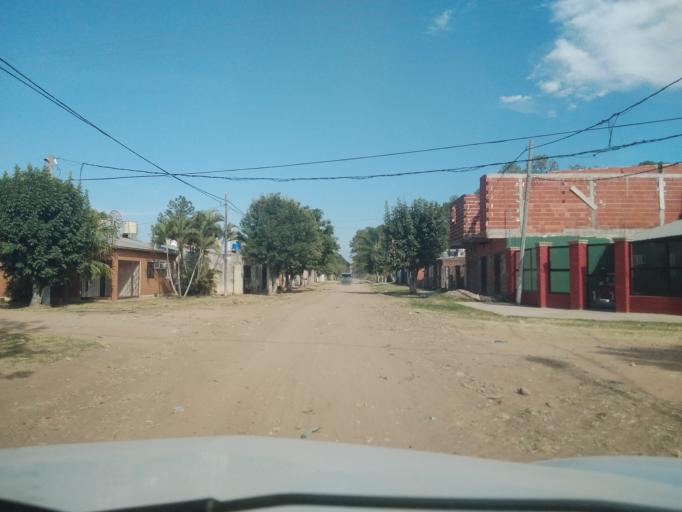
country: AR
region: Corrientes
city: Corrientes
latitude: -27.5093
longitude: -58.8011
